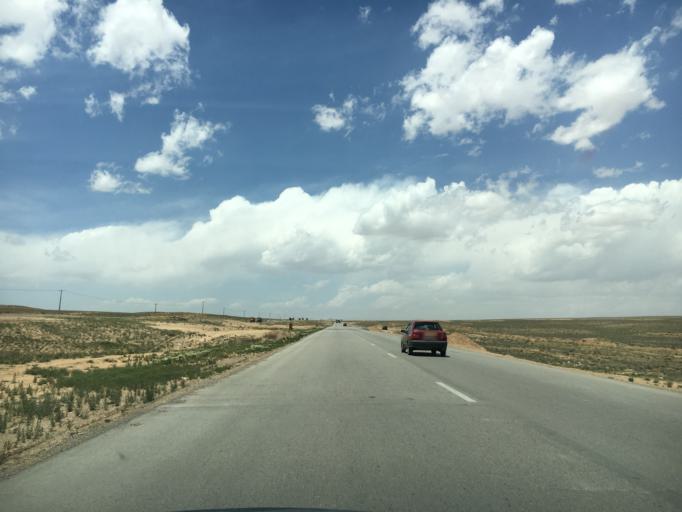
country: IR
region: Markazi
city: Delijan
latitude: 33.5513
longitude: 51.0498
